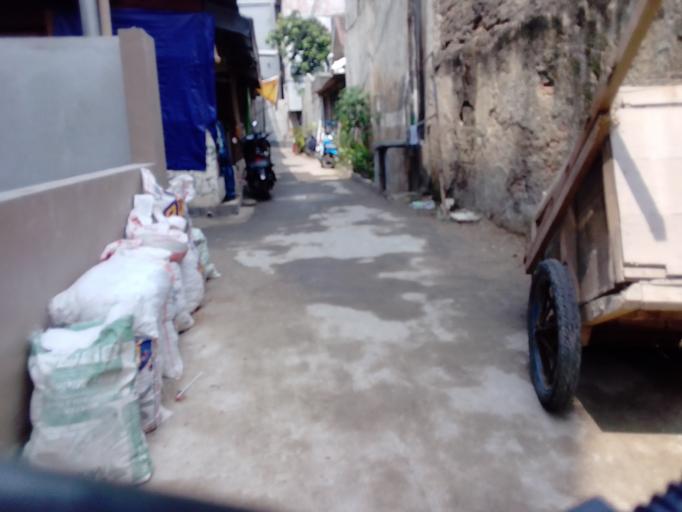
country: ID
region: Jakarta Raya
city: Jakarta
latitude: -6.2138
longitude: 106.8145
